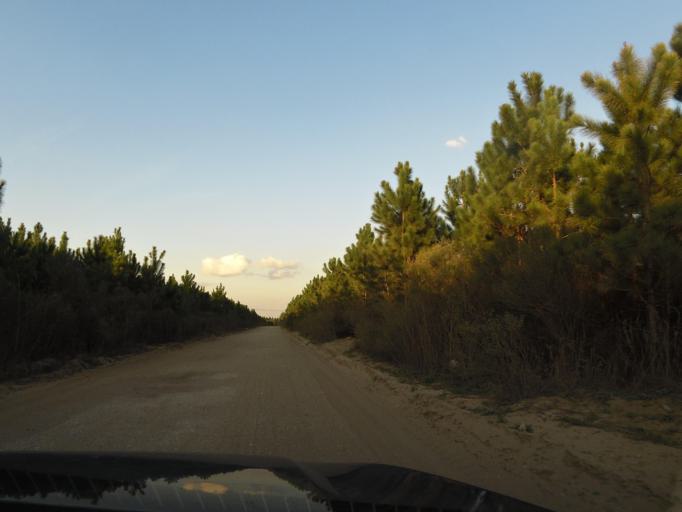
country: US
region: Florida
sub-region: Clay County
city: Keystone Heights
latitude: 29.8171
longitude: -81.8359
